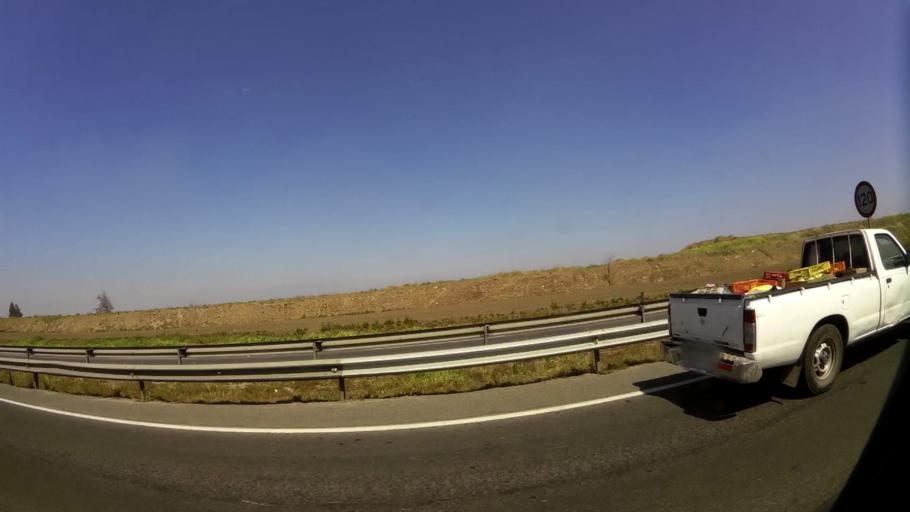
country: CL
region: Santiago Metropolitan
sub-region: Provincia de Santiago
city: Lo Prado
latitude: -33.4969
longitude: -70.7834
